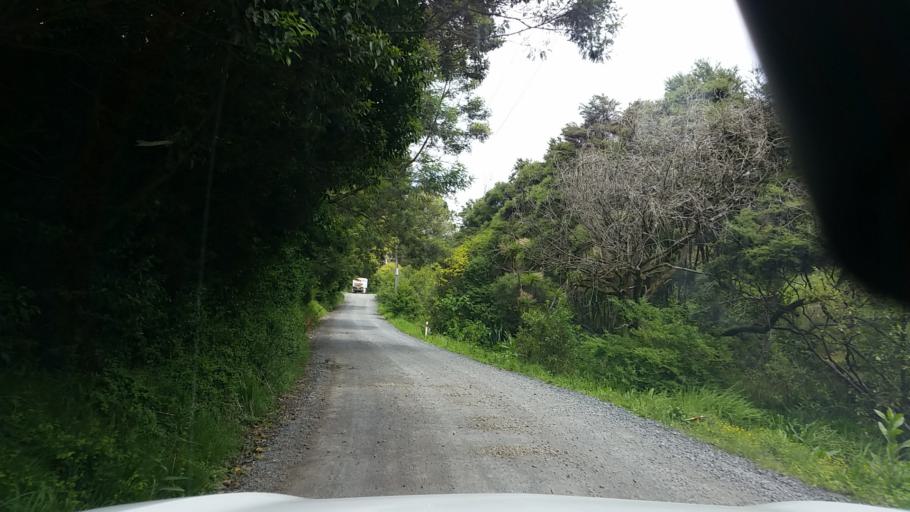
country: NZ
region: Auckland
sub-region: Auckland
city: Rosebank
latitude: -36.8506
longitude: 174.5934
